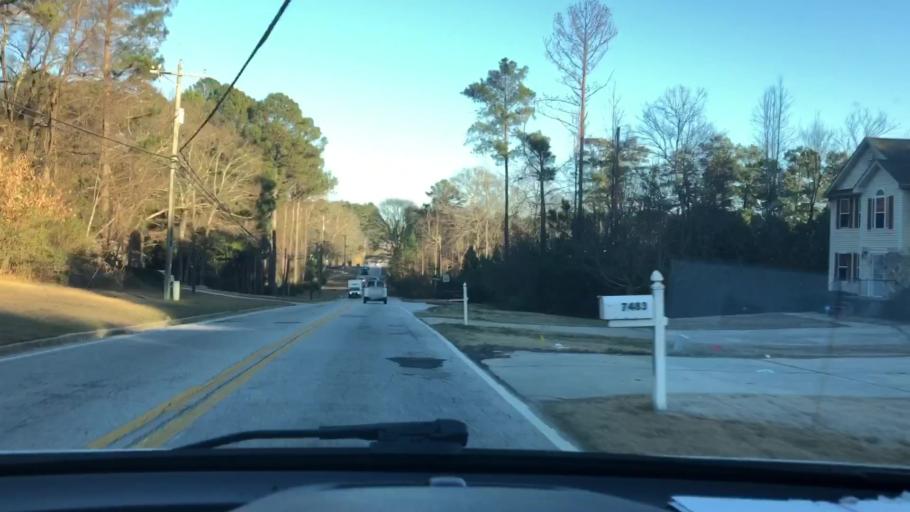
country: US
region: Georgia
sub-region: DeKalb County
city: Lithonia
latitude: 33.7347
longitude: -84.0824
